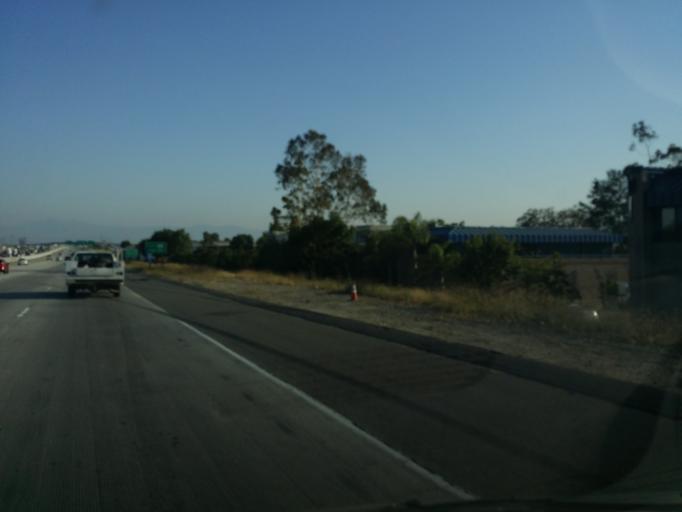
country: US
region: California
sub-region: San Bernardino County
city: Rancho Cucamonga
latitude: 34.0862
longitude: -117.5449
